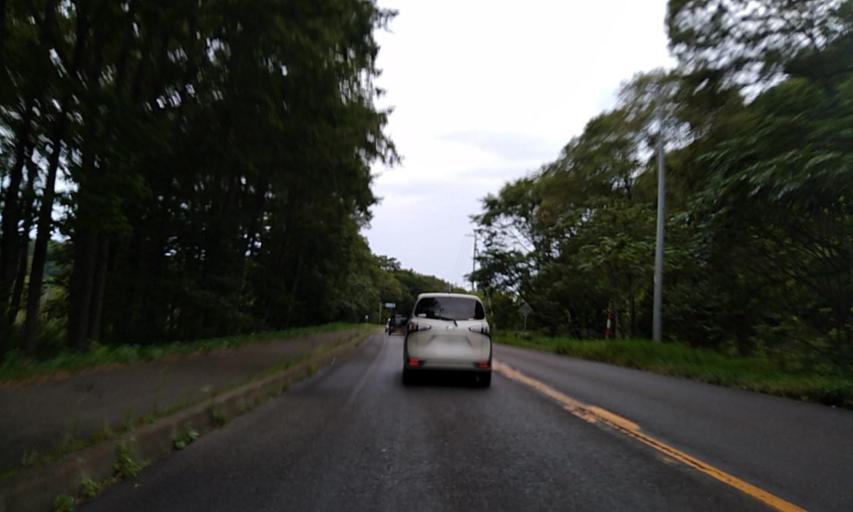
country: JP
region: Hokkaido
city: Abashiri
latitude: 43.9753
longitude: 144.2179
